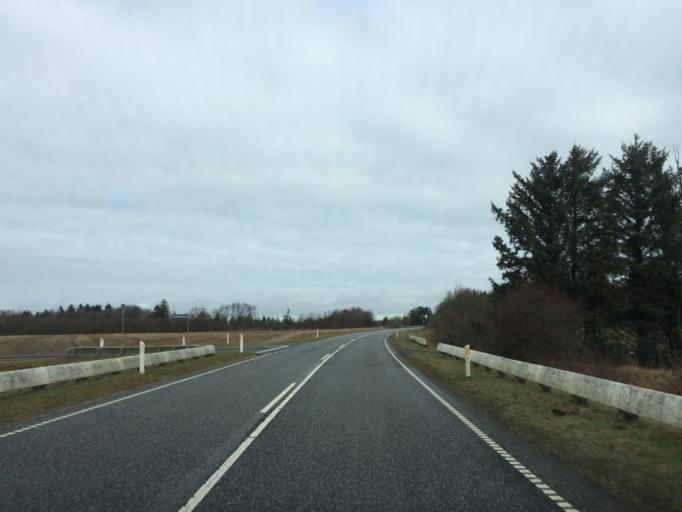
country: DK
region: Central Jutland
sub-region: Holstebro Kommune
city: Ulfborg
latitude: 56.3708
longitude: 8.4406
